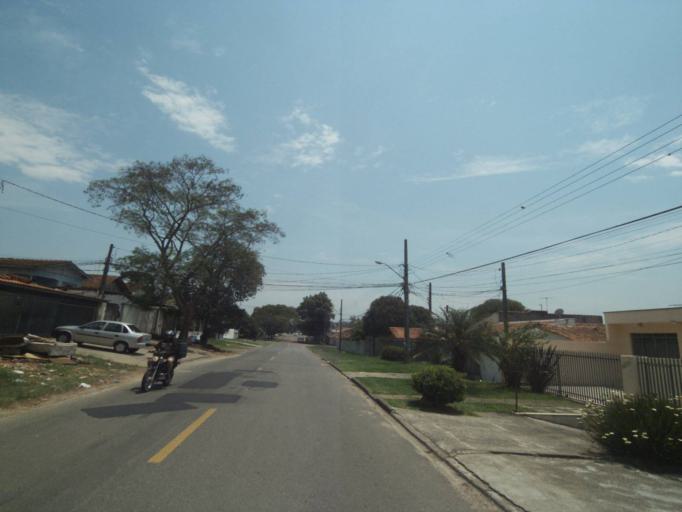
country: BR
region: Parana
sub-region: Pinhais
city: Pinhais
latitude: -25.4090
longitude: -49.2067
